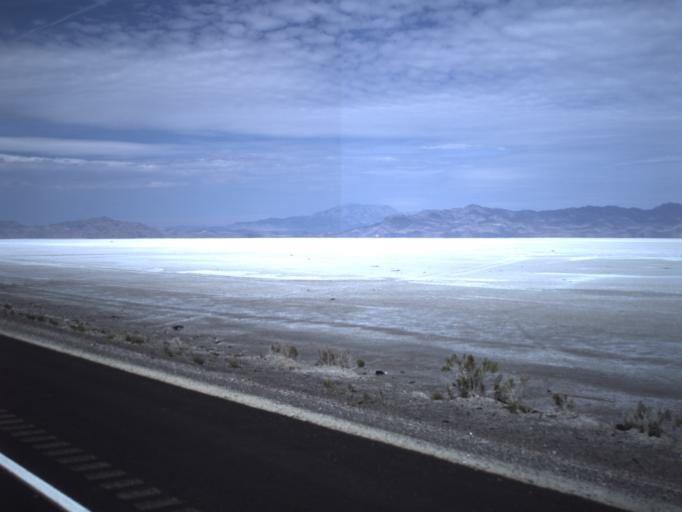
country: US
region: Utah
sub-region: Tooele County
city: Wendover
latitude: 40.7344
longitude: -113.6160
